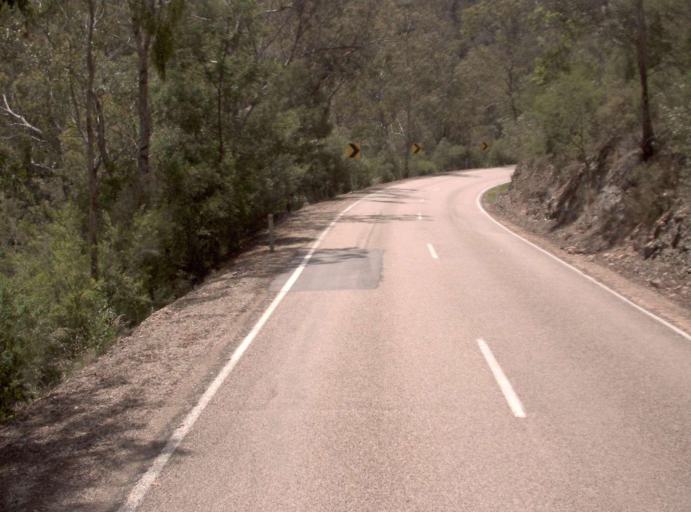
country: AU
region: Victoria
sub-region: East Gippsland
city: Lakes Entrance
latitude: -37.5345
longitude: 147.8607
